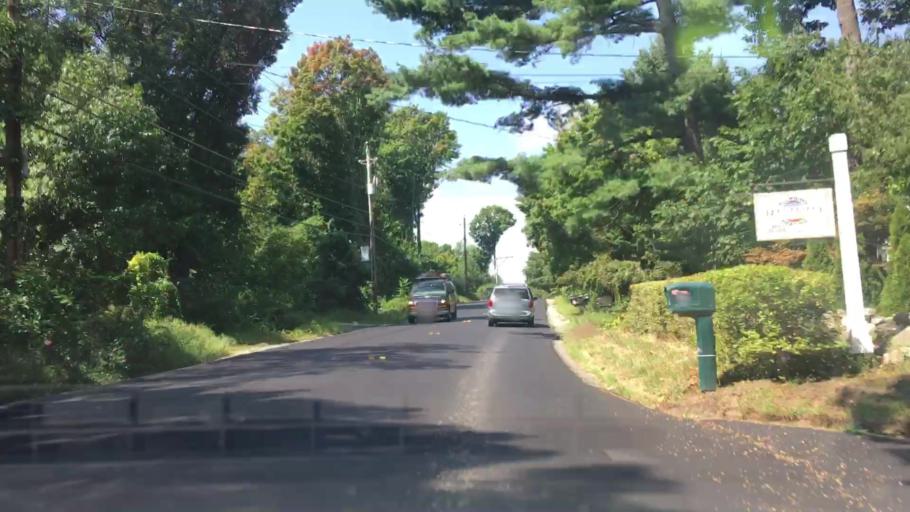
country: US
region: New Hampshire
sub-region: Rockingham County
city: Hampstead
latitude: 42.8930
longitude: -71.2081
